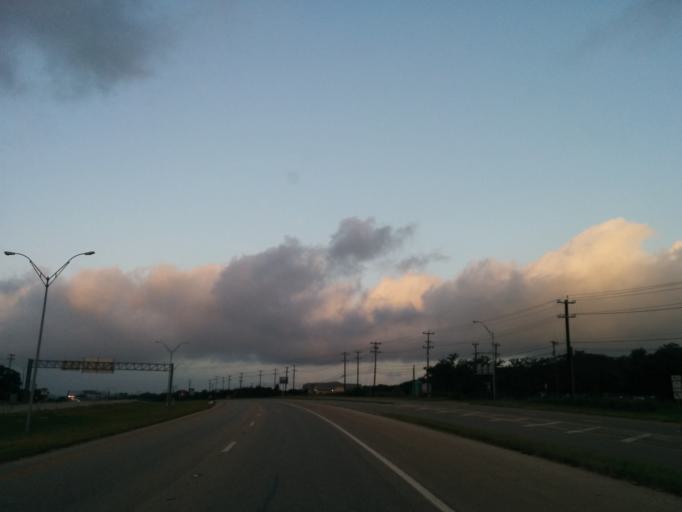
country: US
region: Texas
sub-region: Bexar County
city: Helotes
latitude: 29.5860
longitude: -98.6364
